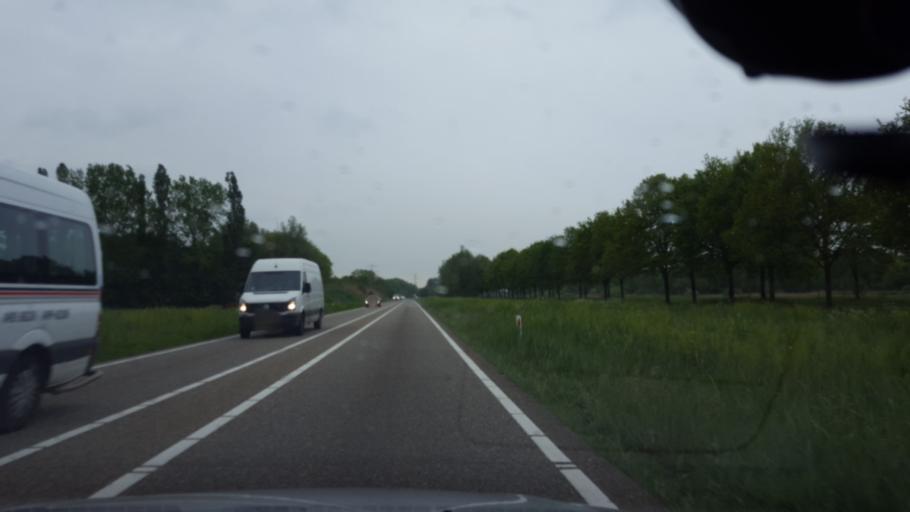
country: NL
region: North Brabant
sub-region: Gemeente Helmond
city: Helmond
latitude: 51.5061
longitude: 5.6701
